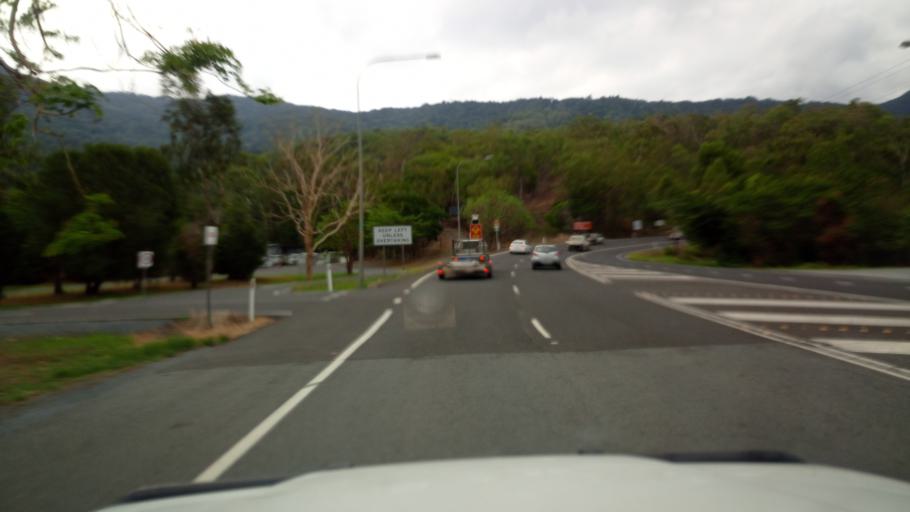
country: AU
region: Queensland
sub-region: Cairns
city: Redlynch
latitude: -16.8390
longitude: 145.6881
